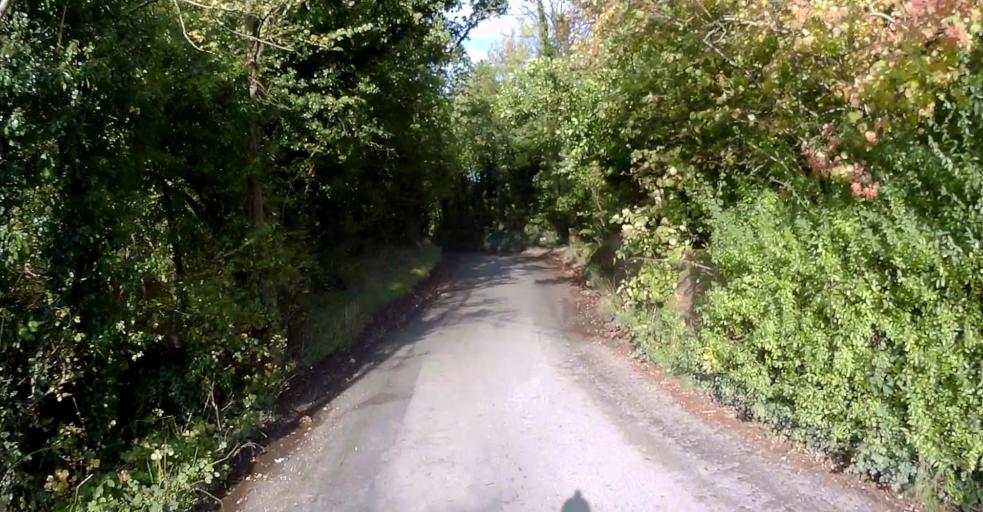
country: GB
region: England
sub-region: Surrey
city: Farnham
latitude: 51.2052
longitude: -0.8270
